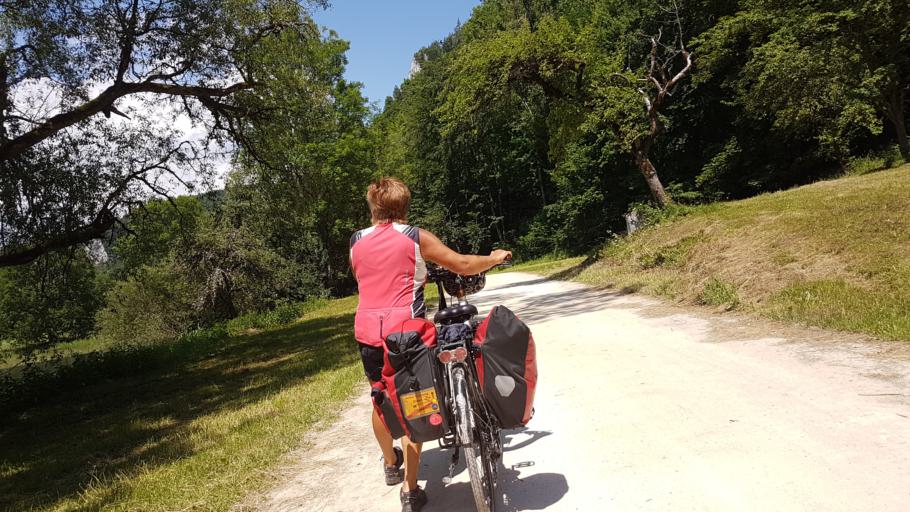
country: DE
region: Baden-Wuerttemberg
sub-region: Freiburg Region
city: Buchheim
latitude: 48.0227
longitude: 8.9653
